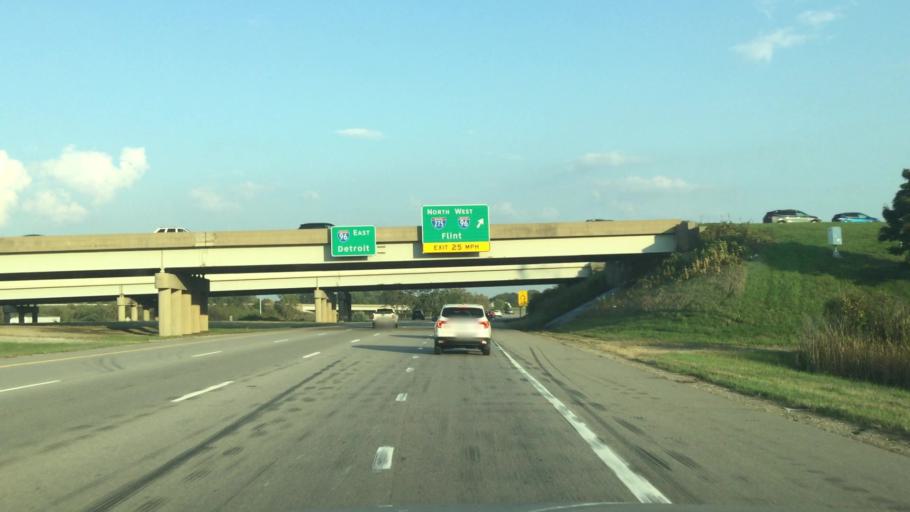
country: US
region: Michigan
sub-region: Wayne County
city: Plymouth
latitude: 42.3864
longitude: -83.4381
